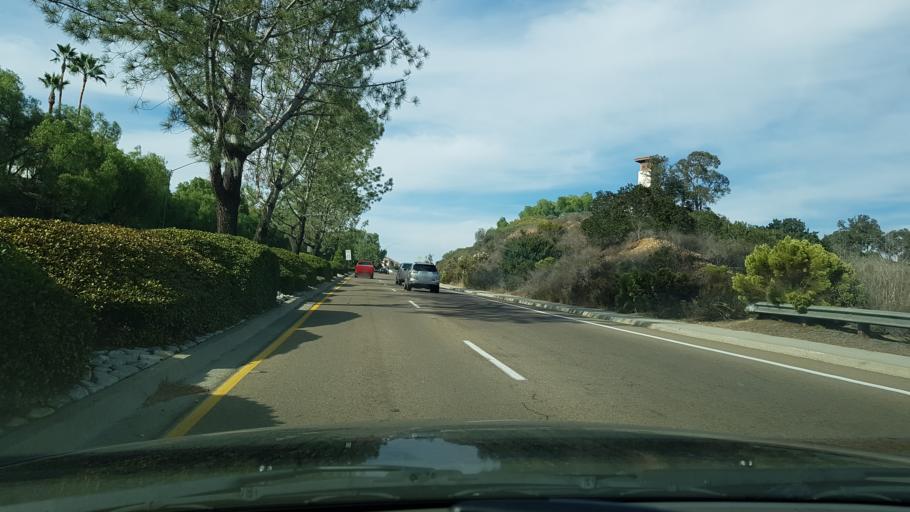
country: US
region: California
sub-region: San Diego County
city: Fairbanks Ranch
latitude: 32.9493
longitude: -117.1298
